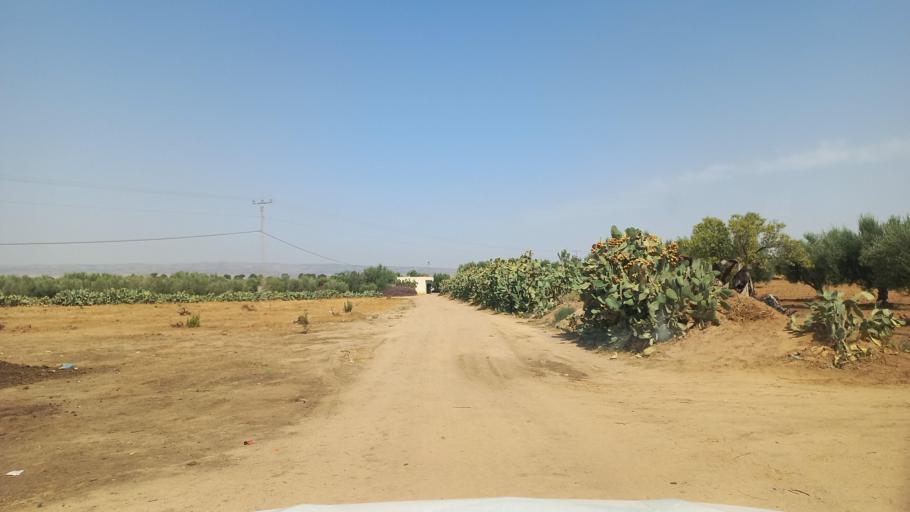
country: TN
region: Al Qasrayn
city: Kasserine
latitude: 35.2539
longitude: 9.0457
